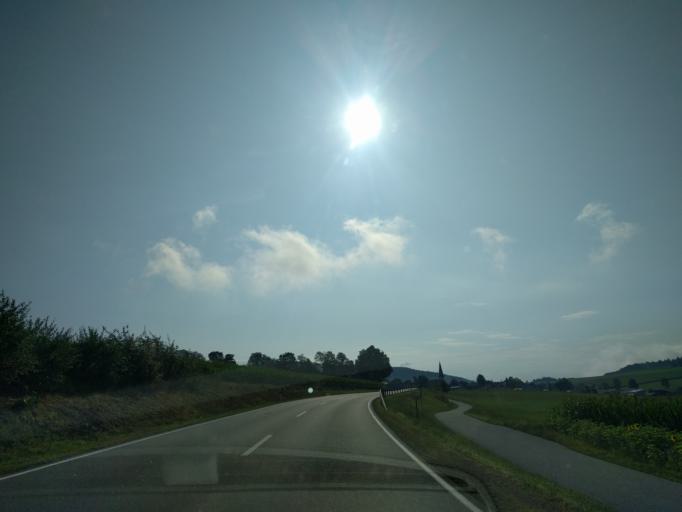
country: DE
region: Bavaria
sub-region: Lower Bavaria
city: Grafenau
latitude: 48.8507
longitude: 13.4213
